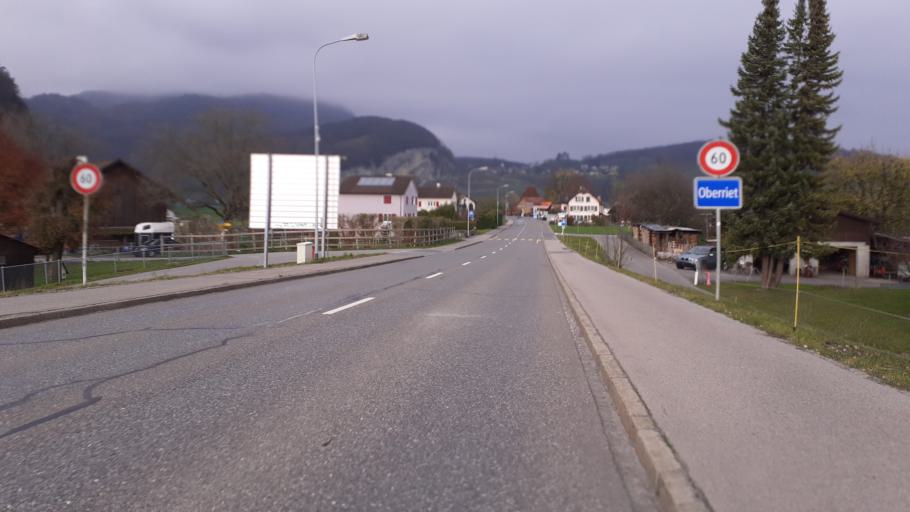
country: CH
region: Saint Gallen
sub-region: Wahlkreis Rheintal
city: Oberriet
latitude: 47.3092
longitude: 9.5664
